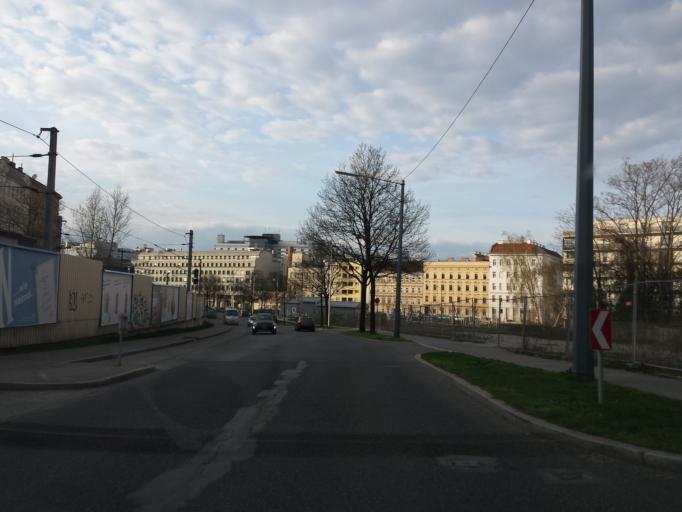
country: AT
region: Vienna
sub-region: Wien Stadt
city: Vienna
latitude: 48.1904
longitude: 16.3919
